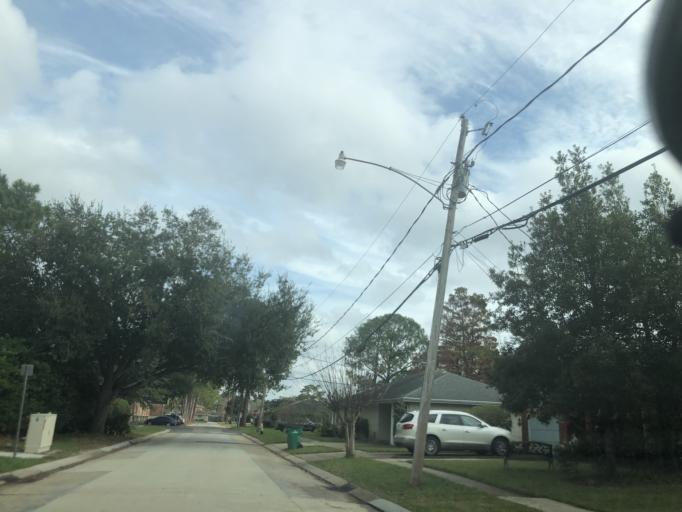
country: US
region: Louisiana
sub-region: Jefferson Parish
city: Metairie
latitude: 29.9894
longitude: -90.1608
